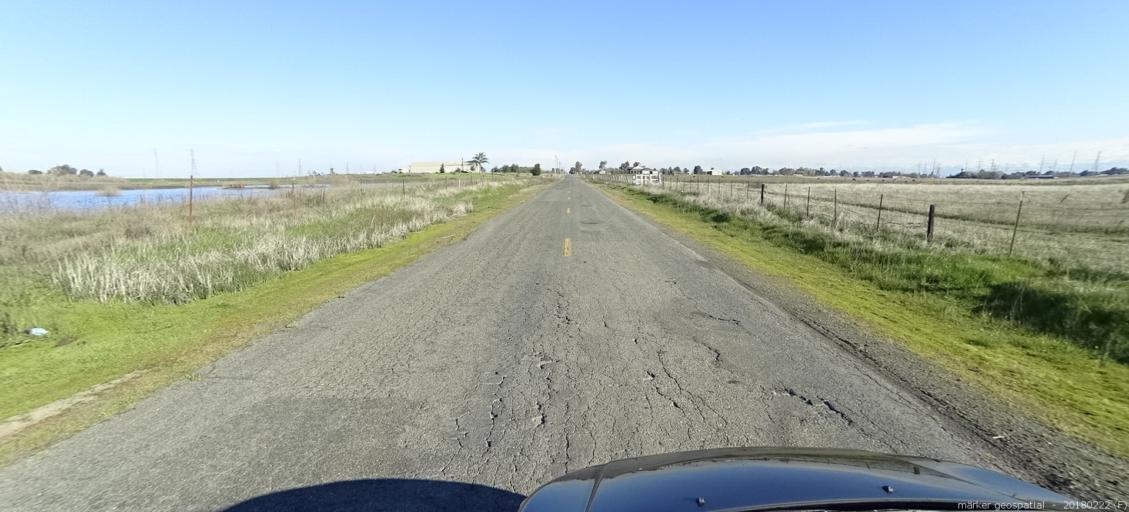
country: US
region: California
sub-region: Sacramento County
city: Elverta
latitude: 38.7191
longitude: -121.4845
